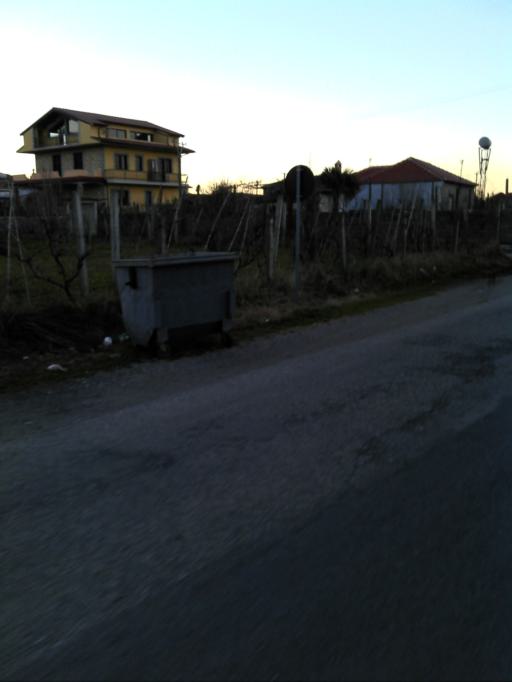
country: AL
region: Shkoder
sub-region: Rrethi i Shkodres
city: Berdica e Madhe
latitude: 42.0141
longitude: 19.4815
